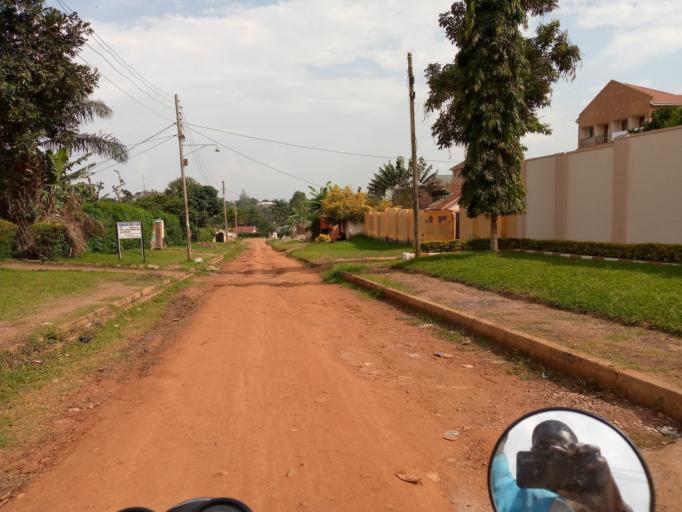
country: UG
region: Eastern Region
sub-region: Mbale District
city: Mbale
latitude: 1.0789
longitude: 34.1705
